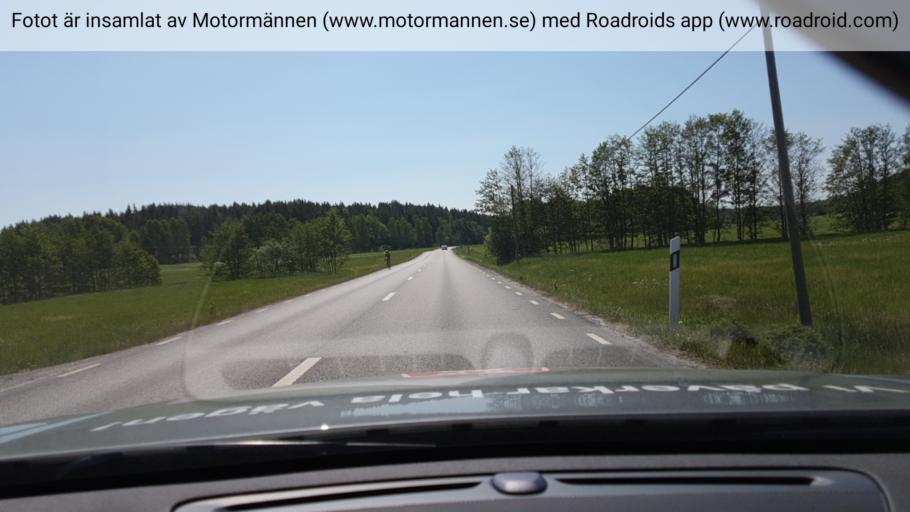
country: SE
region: Stockholm
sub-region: Norrtalje Kommun
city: Rimbo
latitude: 59.6584
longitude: 18.3404
